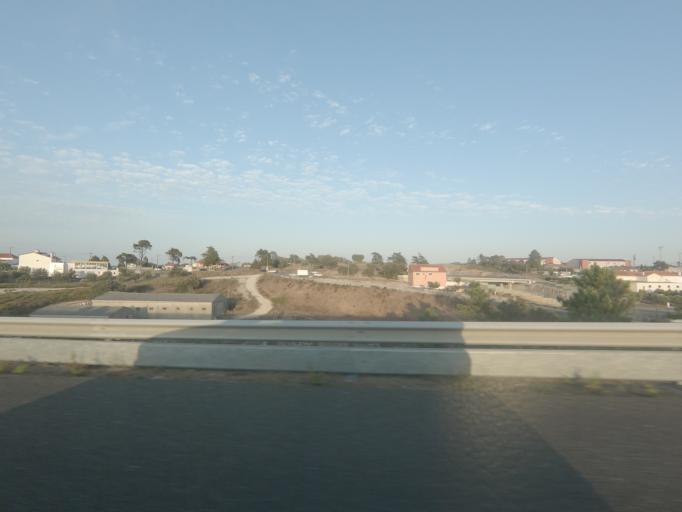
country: PT
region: Leiria
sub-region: Leiria
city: Santa Catarina da Serra
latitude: 39.6705
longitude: -8.6860
